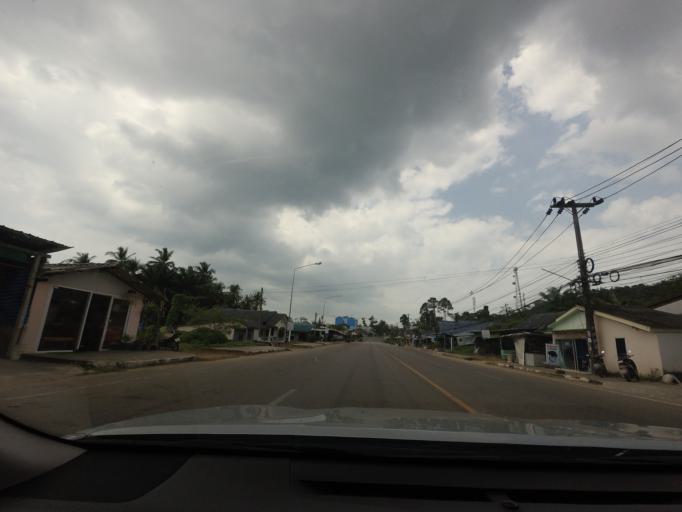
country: TH
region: Phangnga
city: Ban Ao Nang
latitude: 8.0529
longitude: 98.7596
